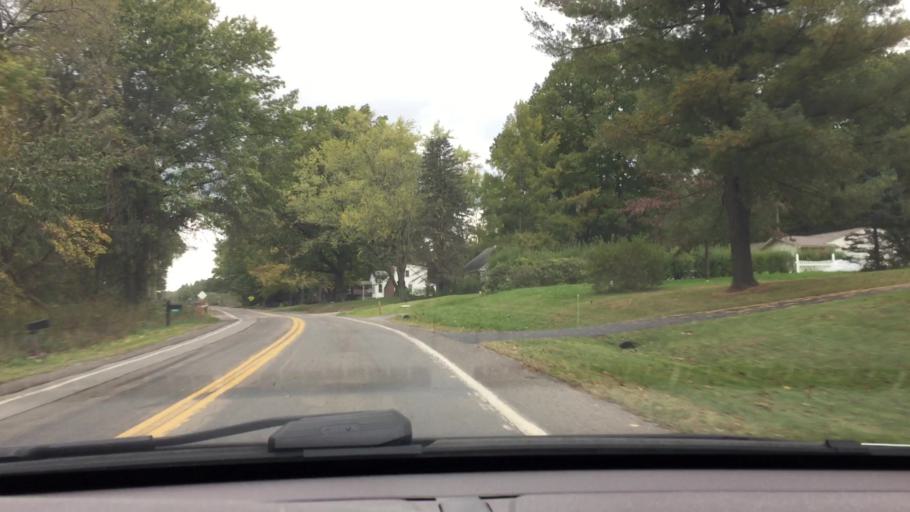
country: US
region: Pennsylvania
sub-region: Lawrence County
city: Oakwood
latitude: 41.0231
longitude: -80.4404
